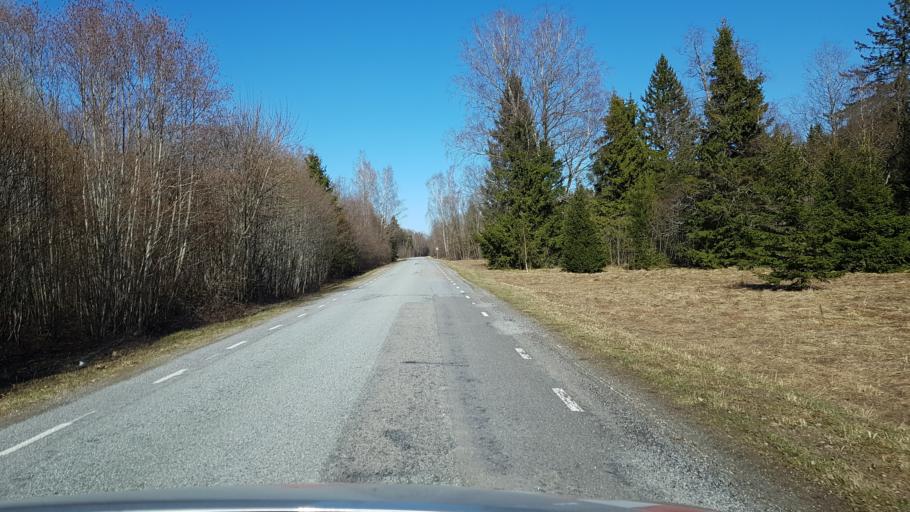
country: EE
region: Laeaene-Virumaa
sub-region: Someru vald
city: Someru
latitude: 59.3863
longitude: 26.4701
